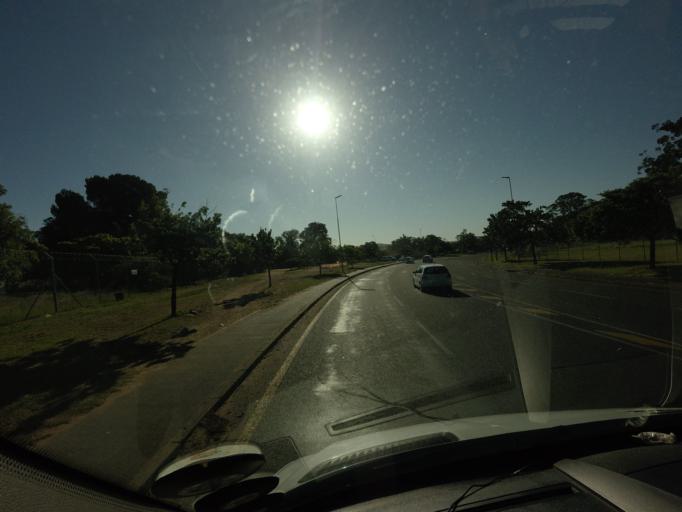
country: ZA
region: Western Cape
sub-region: Cape Winelands District Municipality
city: Stellenbosch
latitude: -33.9249
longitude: 18.8723
